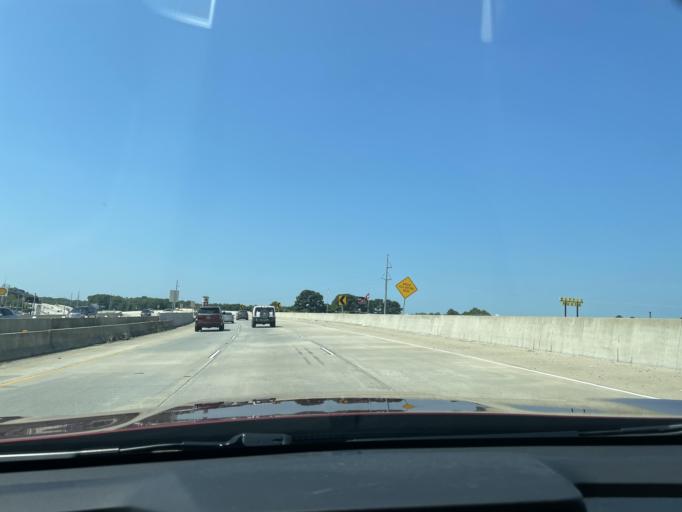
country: US
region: Arkansas
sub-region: Pulaski County
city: Jacksonville
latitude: 34.8692
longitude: -92.1264
